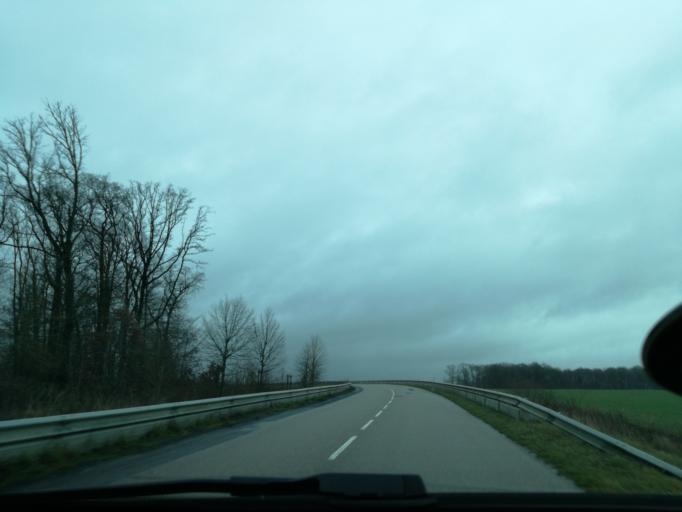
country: FR
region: Lorraine
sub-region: Departement de la Meuse
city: Clermont-en-Argonne
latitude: 48.9928
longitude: 5.0820
